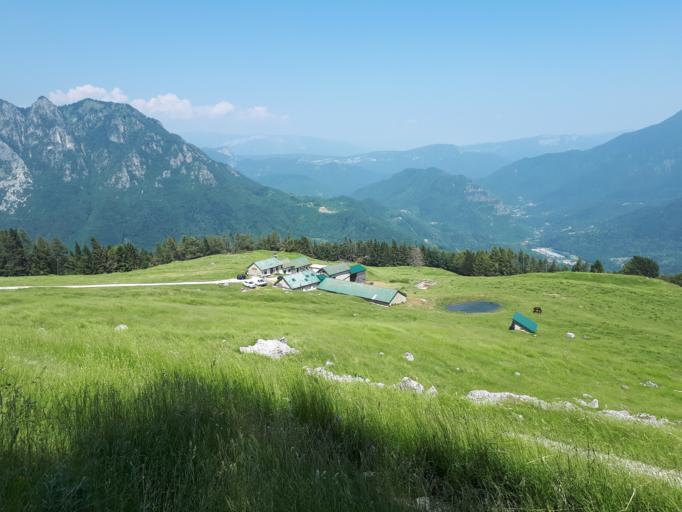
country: IT
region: Veneto
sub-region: Provincia di Vicenza
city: Posina
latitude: 45.7861
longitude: 11.2247
